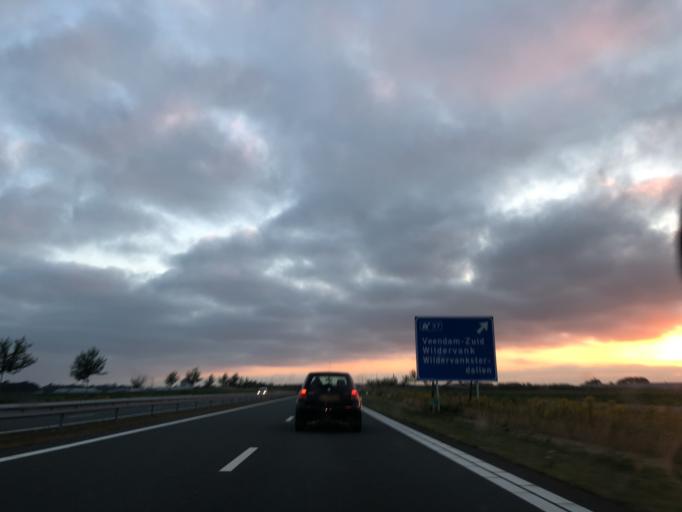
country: NL
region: Groningen
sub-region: Gemeente Veendam
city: Veendam
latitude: 53.0724
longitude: 6.8791
